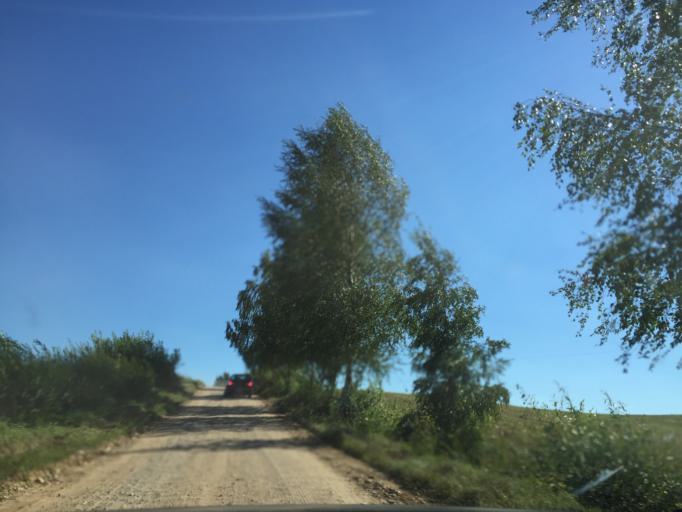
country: LT
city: Zarasai
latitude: 55.7937
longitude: 25.9531
